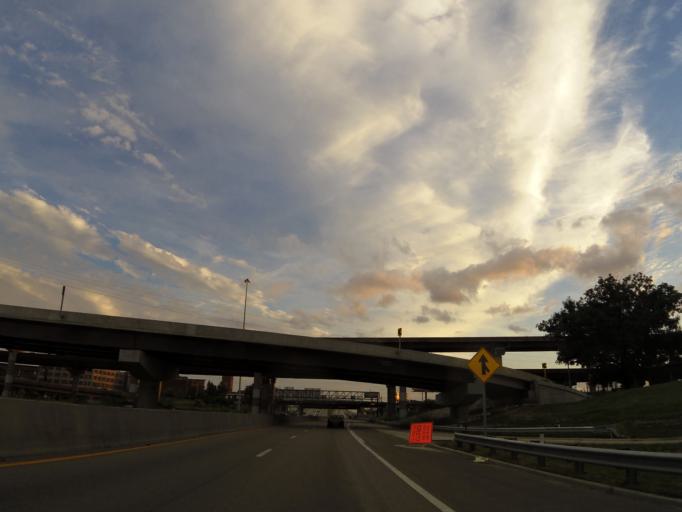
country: US
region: Missouri
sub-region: City of Saint Louis
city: St. Louis
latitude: 38.6209
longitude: -90.1892
